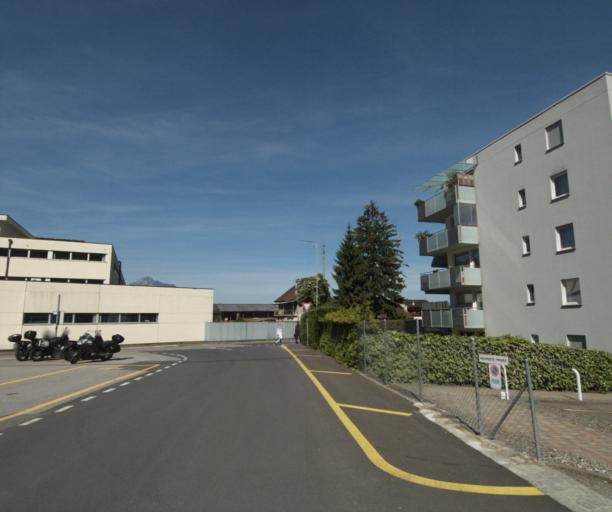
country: CH
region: Vaud
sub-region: Aigle District
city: Villeneuve
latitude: 46.3947
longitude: 6.9349
